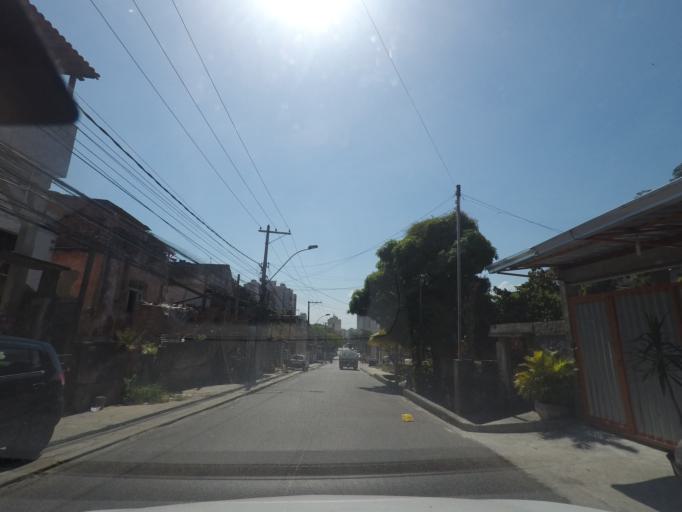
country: BR
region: Rio de Janeiro
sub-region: Niteroi
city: Niteroi
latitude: -22.9061
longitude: -43.0831
